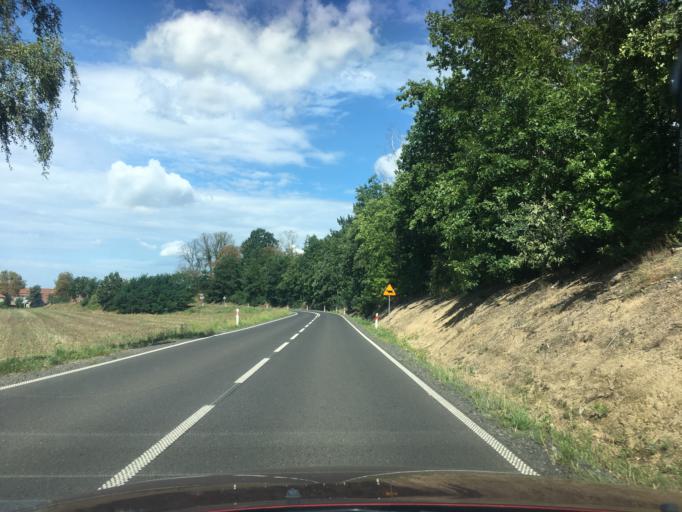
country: PL
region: Lower Silesian Voivodeship
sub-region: Powiat zgorzelecki
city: Piensk
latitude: 51.2094
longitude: 15.0227
